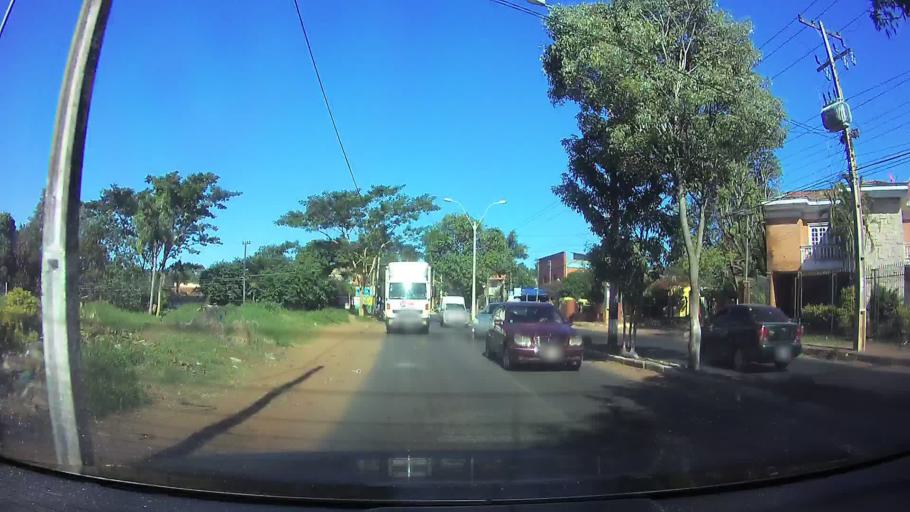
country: PY
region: Central
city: Villa Elisa
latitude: -25.3660
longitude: -57.5783
